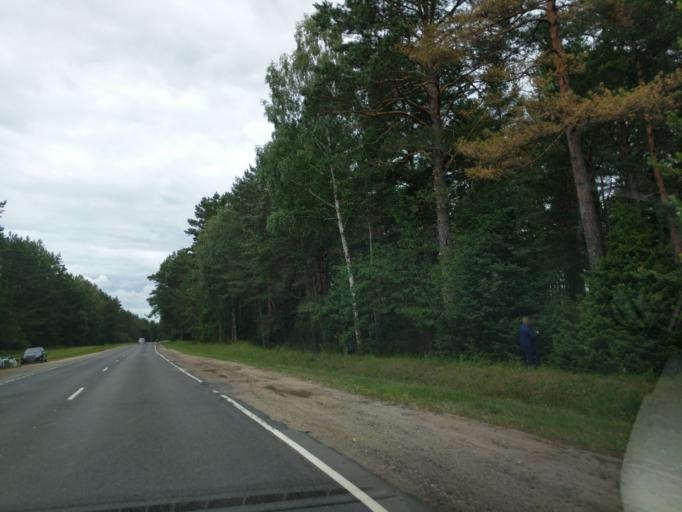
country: BY
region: Minsk
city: Myadzyel
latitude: 54.8367
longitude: 26.9342
